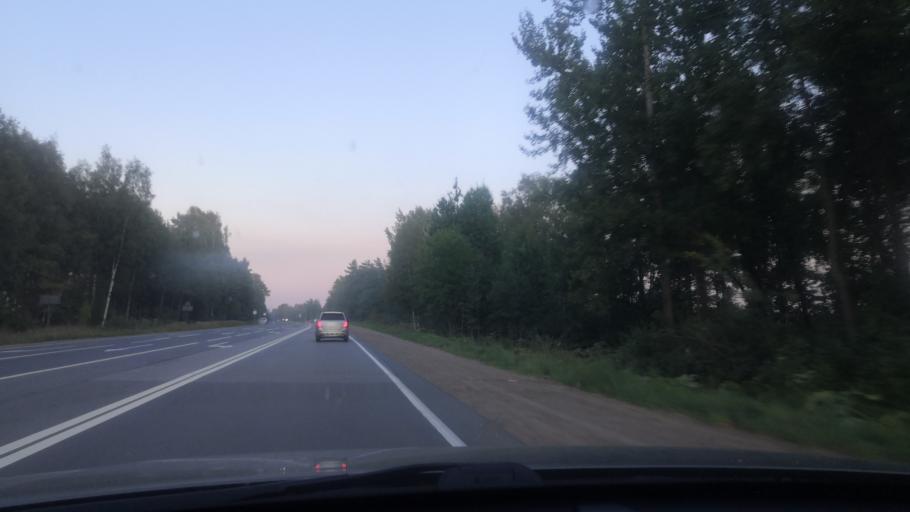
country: RU
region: St.-Petersburg
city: Beloostrov
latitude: 60.1982
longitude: 30.0083
